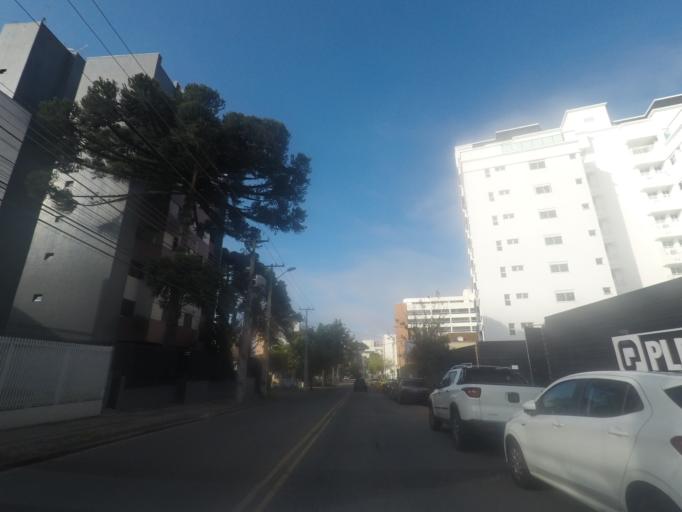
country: BR
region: Parana
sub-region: Curitiba
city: Curitiba
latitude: -25.4085
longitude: -49.2643
